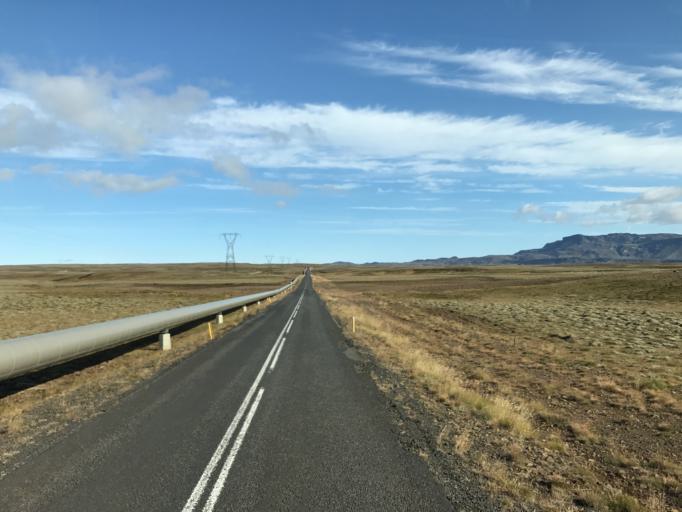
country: IS
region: Capital Region
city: Mosfellsbaer
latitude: 64.1136
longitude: -21.5180
